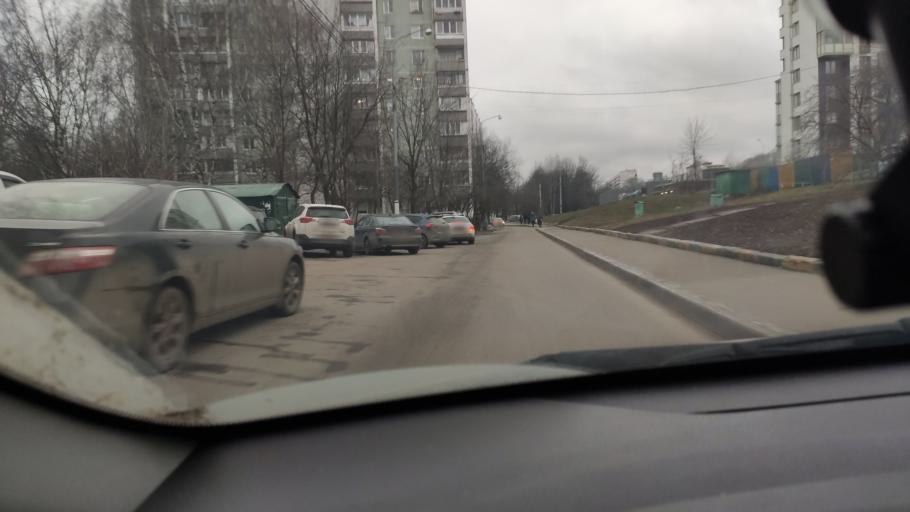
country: RU
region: Moscow
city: Chertanovo Yuzhnoye
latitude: 55.5995
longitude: 37.5910
